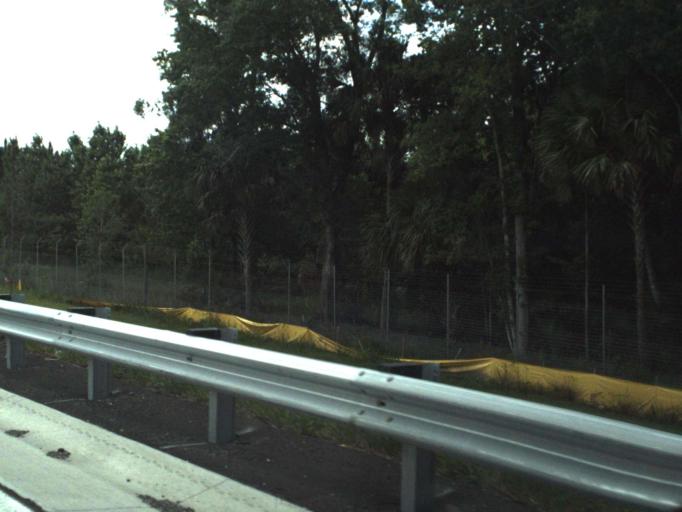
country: US
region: Florida
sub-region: Volusia County
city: South Daytona
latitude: 29.1503
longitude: -81.0882
